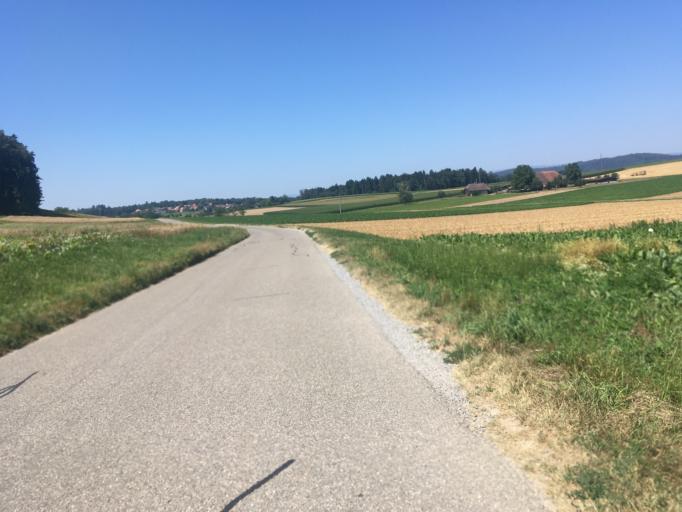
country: CH
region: Bern
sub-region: Bern-Mittelland District
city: Fraubrunnen
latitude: 47.0900
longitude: 7.4912
